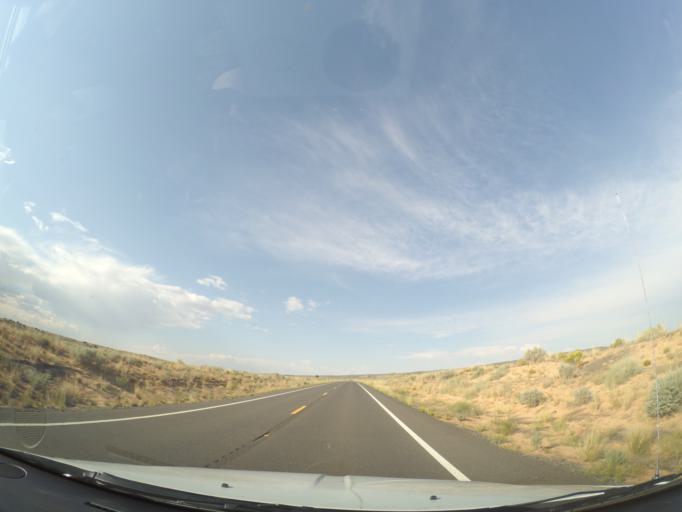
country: US
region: Arizona
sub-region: Coconino County
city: Kaibito
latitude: 36.4784
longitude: -111.4158
